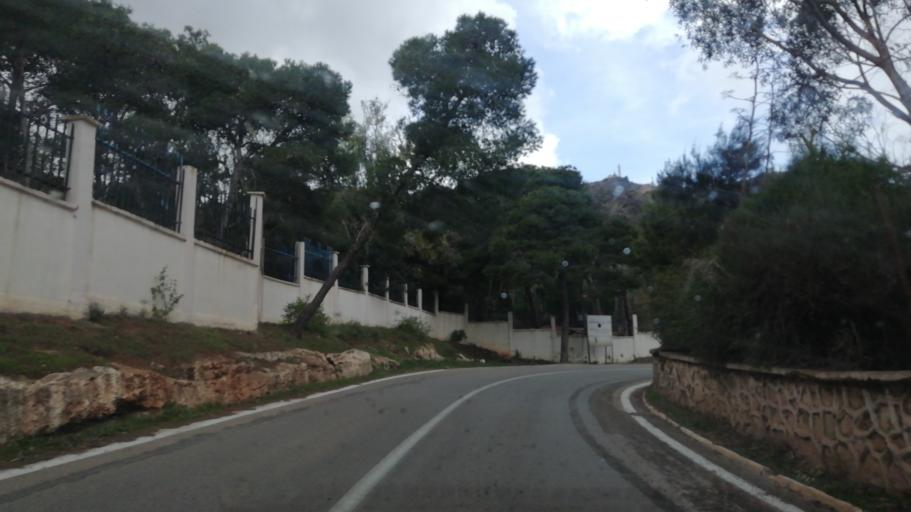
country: DZ
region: Oran
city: Oran
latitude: 35.7021
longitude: -0.6620
